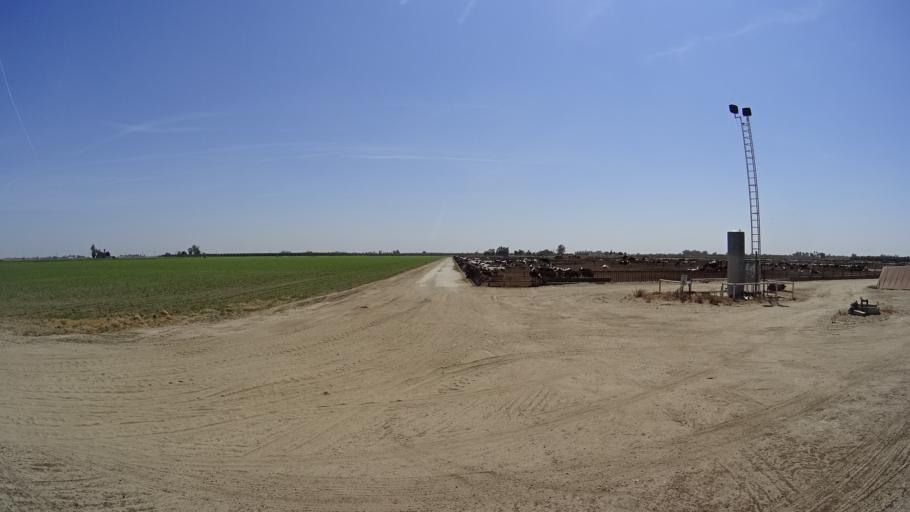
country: US
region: California
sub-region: Fresno County
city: Riverdale
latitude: 36.3959
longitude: -119.8873
